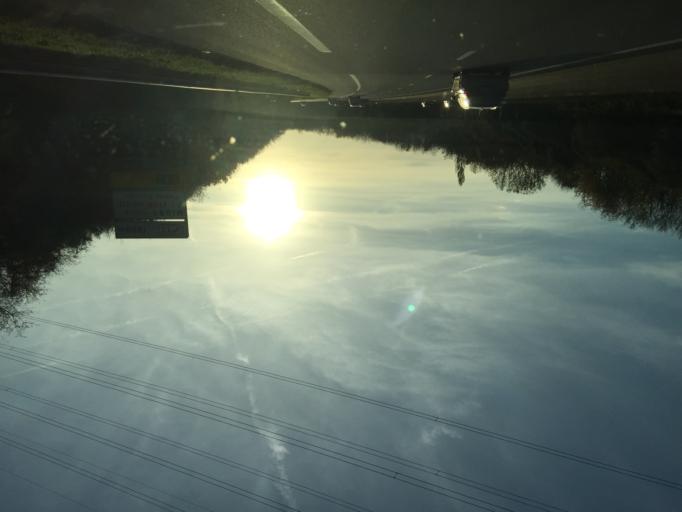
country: FR
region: Rhone-Alpes
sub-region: Departement du Rhone
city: Mions
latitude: 45.6767
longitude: 4.9570
